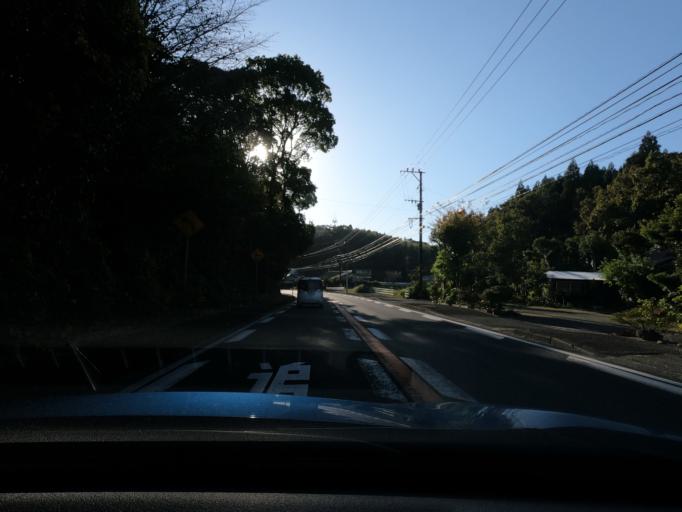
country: JP
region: Kagoshima
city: Akune
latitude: 32.0462
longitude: 130.2172
